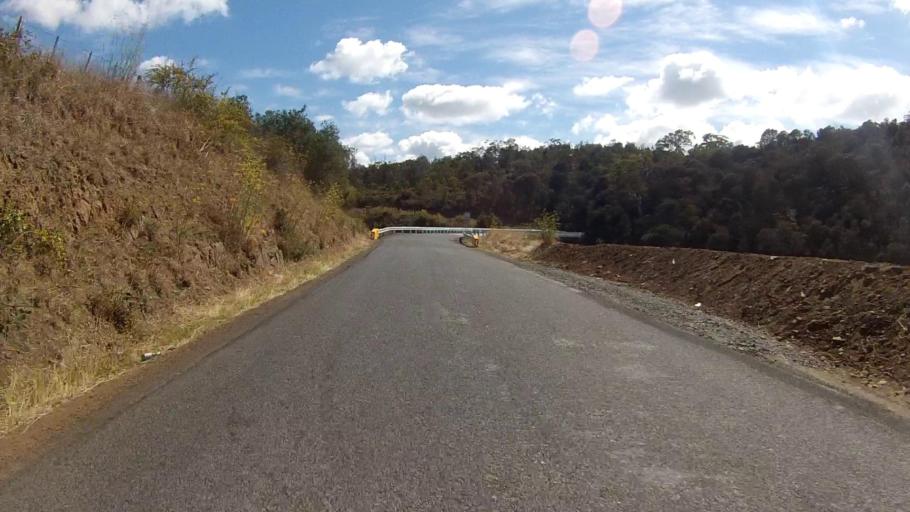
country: AU
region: Tasmania
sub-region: Brighton
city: Bridgewater
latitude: -42.7311
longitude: 147.2618
